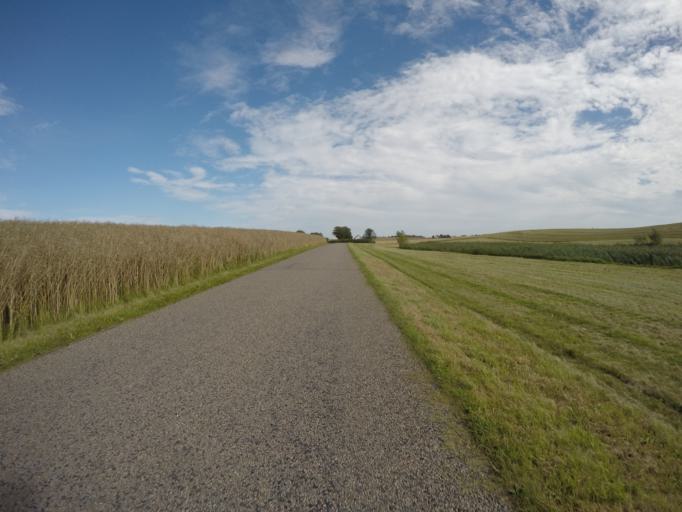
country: SE
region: Skane
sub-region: Simrishamns Kommun
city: Simrishamn
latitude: 55.4976
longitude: 14.2327
